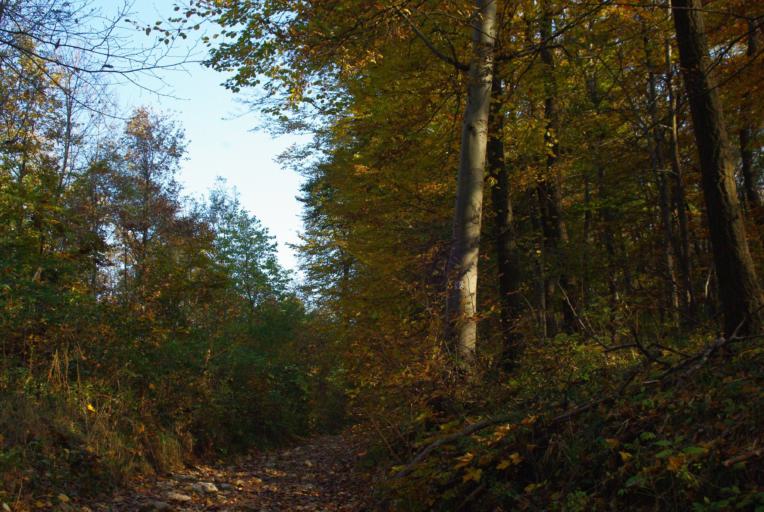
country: HU
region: Pest
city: Piliscsaba
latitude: 47.6530
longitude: 18.8371
